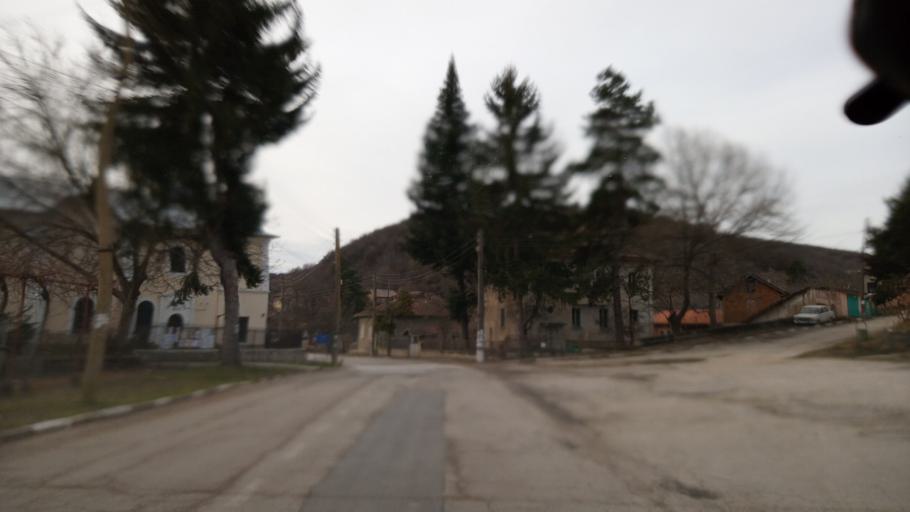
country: BG
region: Pleven
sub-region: Obshtina Belene
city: Belene
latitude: 43.6030
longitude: 24.9973
